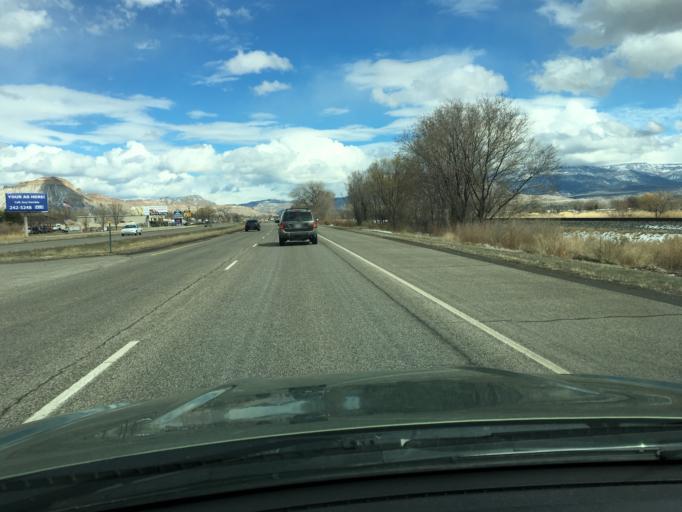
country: US
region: Colorado
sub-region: Mesa County
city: Fruitvale
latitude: 39.0799
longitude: -108.4844
